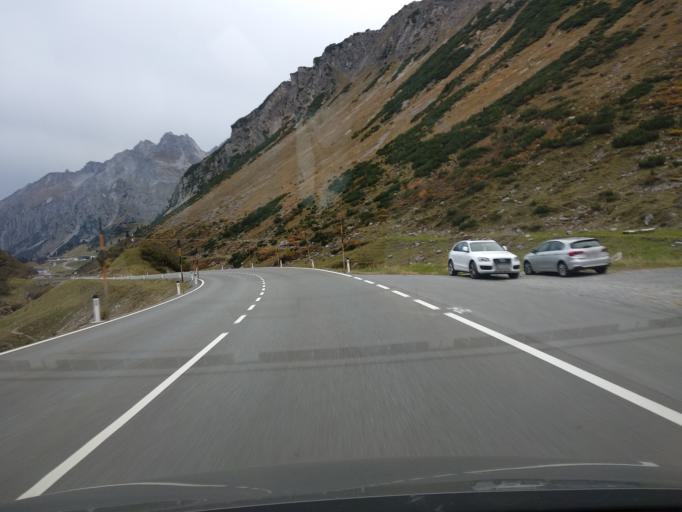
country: AT
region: Tyrol
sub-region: Politischer Bezirk Landeck
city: Sankt Anton am Arlberg
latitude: 47.1357
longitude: 10.2015
